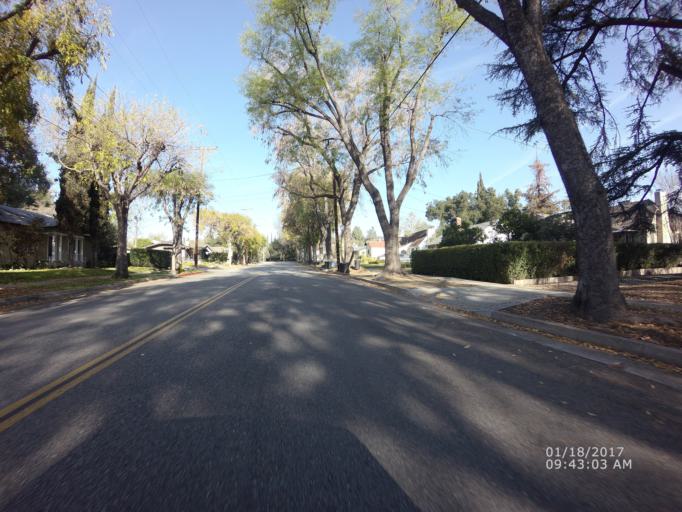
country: US
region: California
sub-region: Los Angeles County
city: South Pasadena
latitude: 34.1170
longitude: -118.1421
